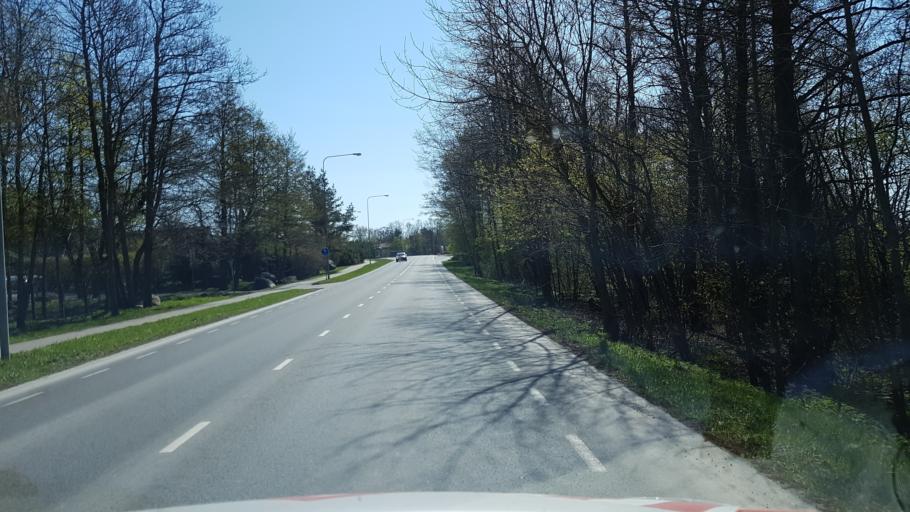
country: EE
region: Harju
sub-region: Viimsi vald
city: Rummu
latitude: 59.5329
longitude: 24.7943
